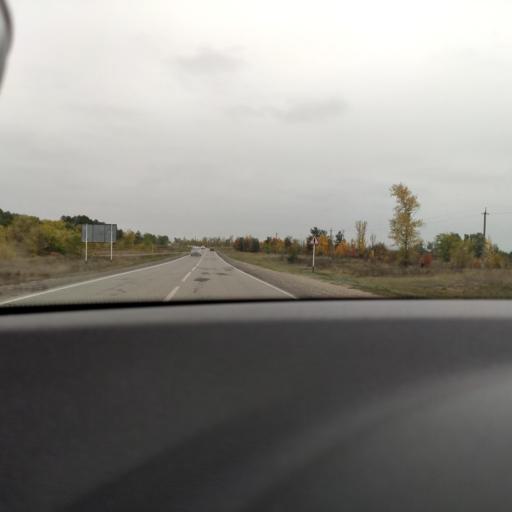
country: RU
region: Samara
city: Mirnyy
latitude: 53.5208
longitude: 50.3230
